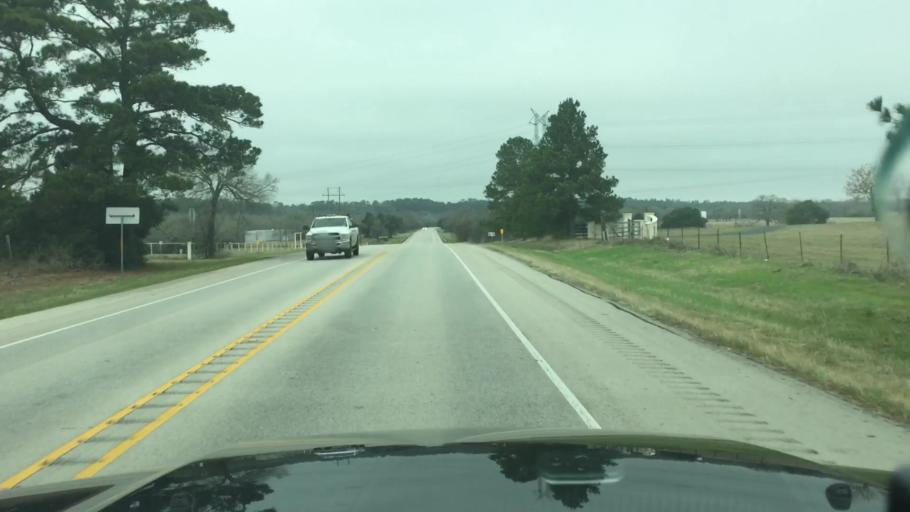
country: US
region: Texas
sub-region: Fayette County
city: La Grange
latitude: 30.0260
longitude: -96.9034
